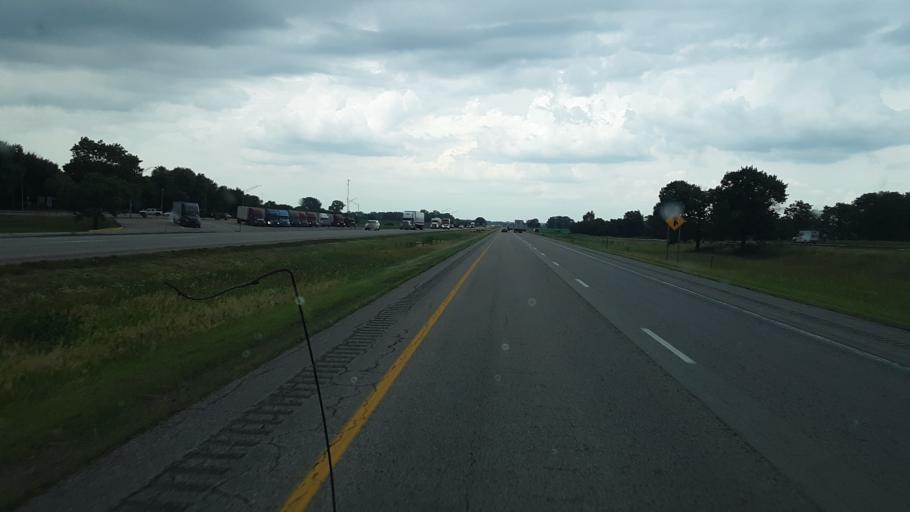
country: US
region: Iowa
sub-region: Pottawattamie County
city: Council Bluffs
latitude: 41.4022
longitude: -95.6590
